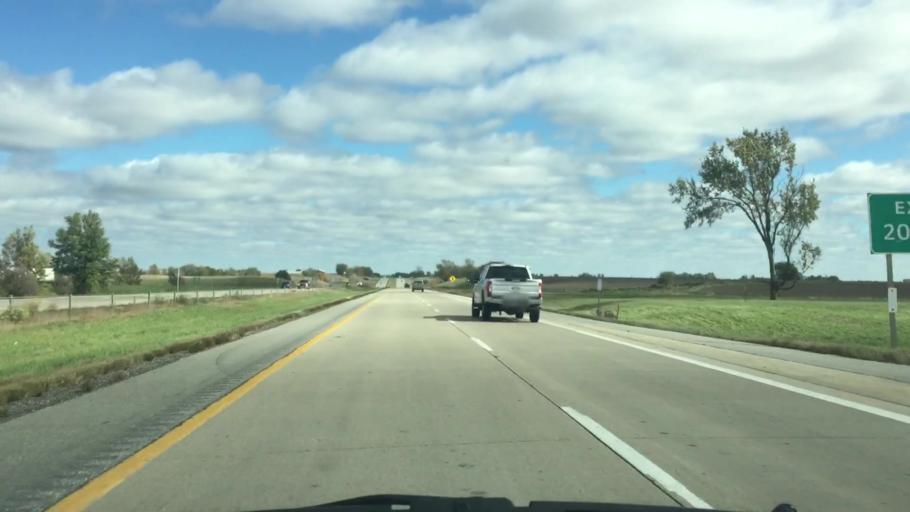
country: US
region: Iowa
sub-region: Poweshiek County
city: Brooklyn
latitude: 41.6954
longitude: -92.3562
